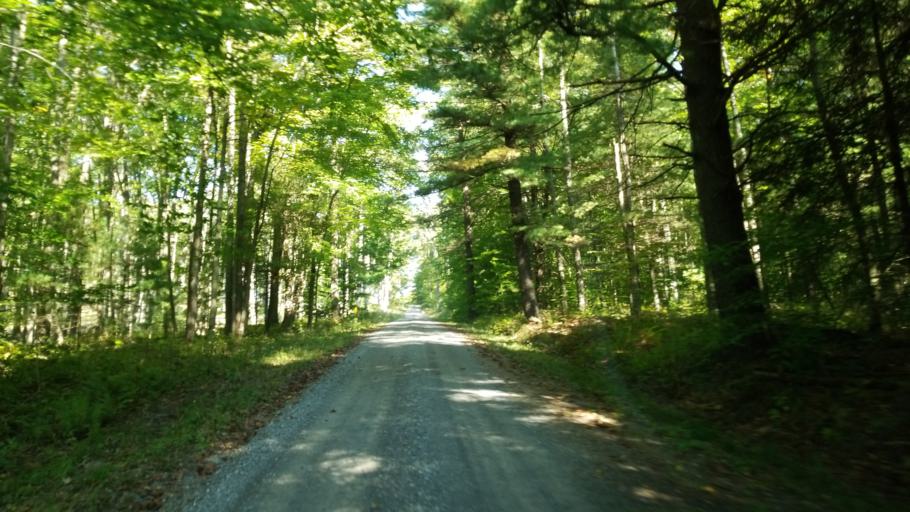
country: US
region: Pennsylvania
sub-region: Clearfield County
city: Treasure Lake
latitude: 41.1380
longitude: -78.5719
